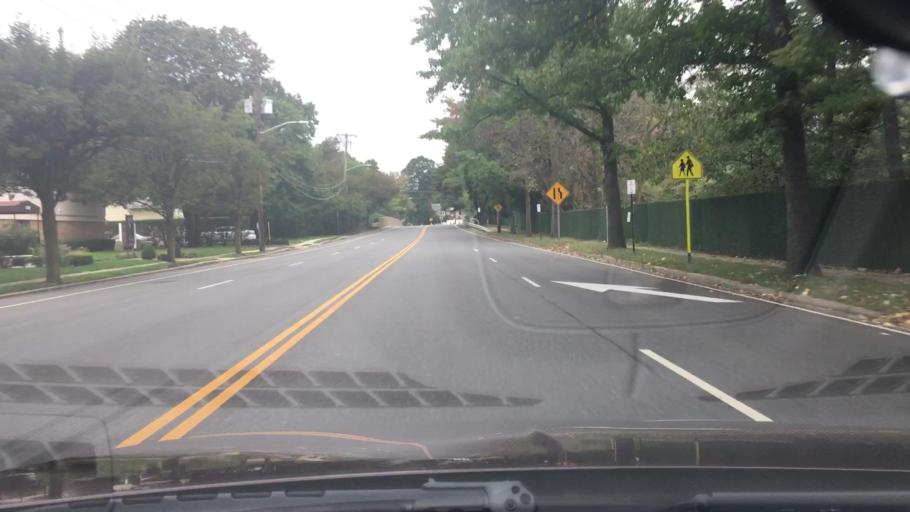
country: US
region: New York
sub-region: Nassau County
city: Jericho
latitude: 40.7726
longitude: -73.5510
